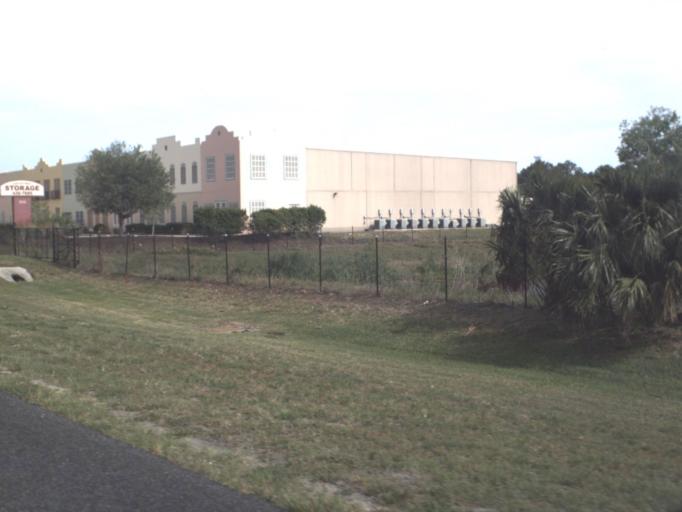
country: US
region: Florida
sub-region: Flagler County
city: Flagler Beach
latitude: 29.4765
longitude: -81.1519
